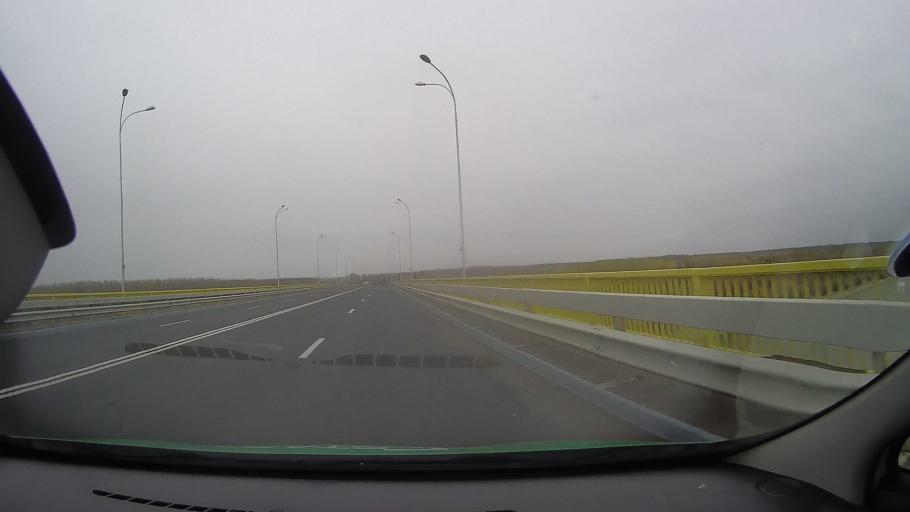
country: RO
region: Ialomita
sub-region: Comuna Giurgeni
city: Giurgeni
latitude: 44.7544
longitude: 27.8757
